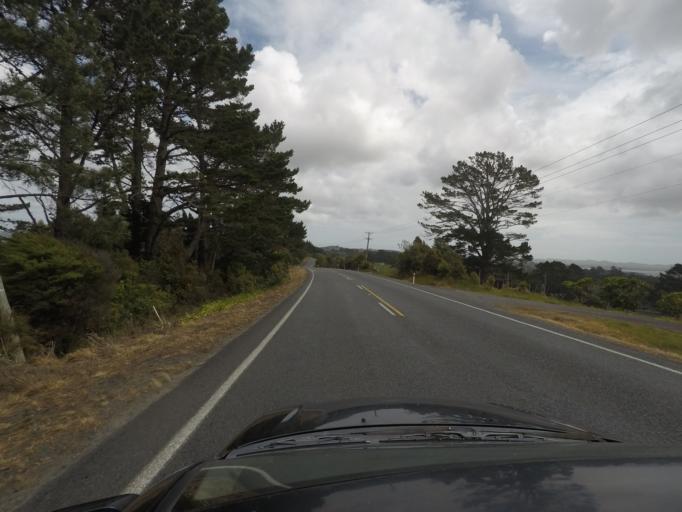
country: NZ
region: Auckland
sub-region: Auckland
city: Parakai
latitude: -36.5921
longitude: 174.4863
